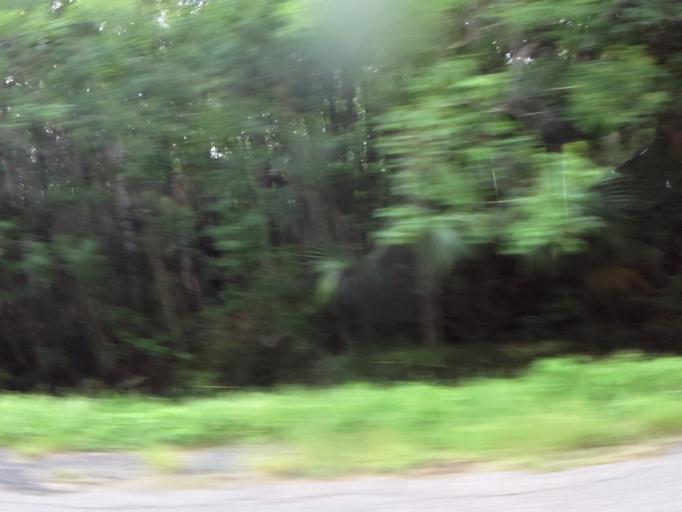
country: US
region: Florida
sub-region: Nassau County
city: Nassau Village-Ratliff
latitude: 30.3938
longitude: -81.7780
